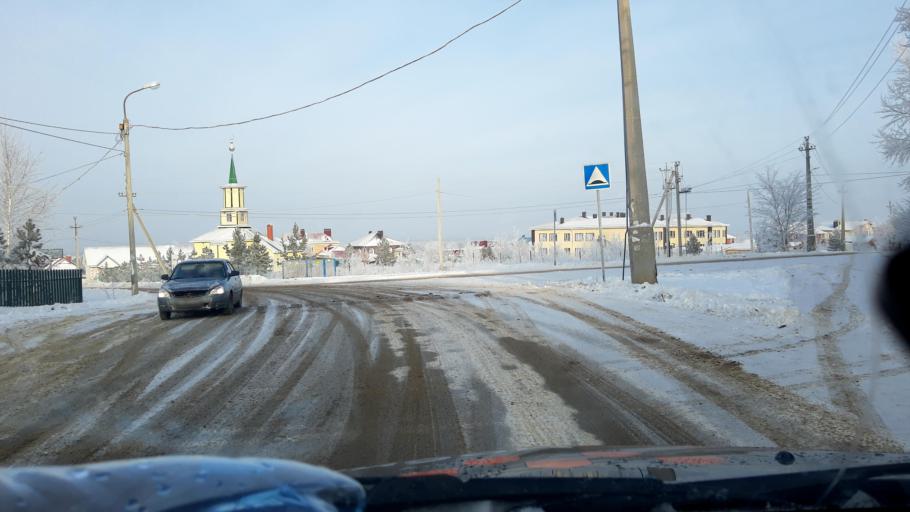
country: RU
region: Bashkortostan
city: Ufa
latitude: 54.5987
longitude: 55.9530
